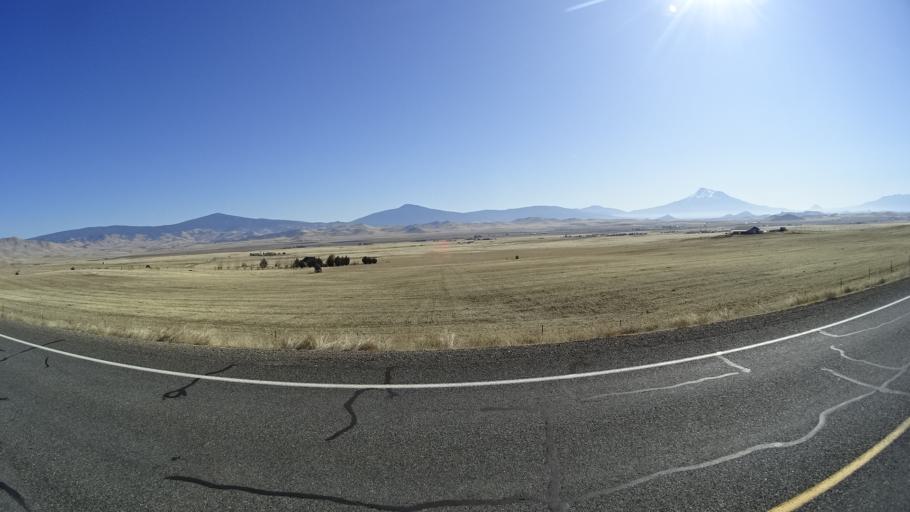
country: US
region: California
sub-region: Siskiyou County
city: Montague
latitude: 41.7968
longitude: -122.5111
